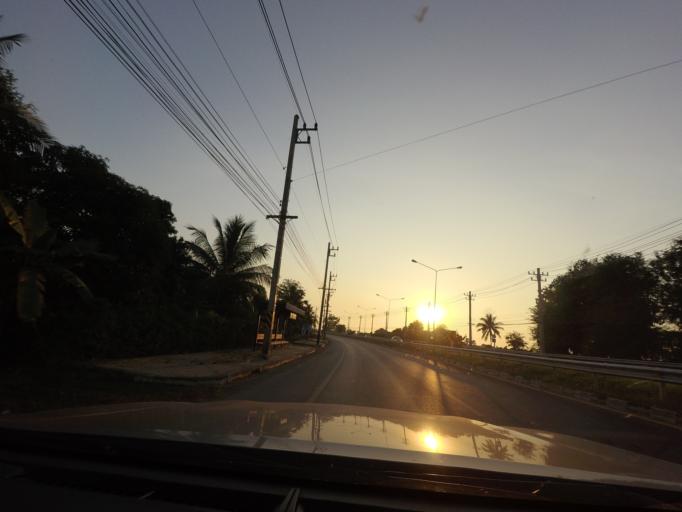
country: TH
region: Sukhothai
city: Si Samrong
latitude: 17.1102
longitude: 99.8442
